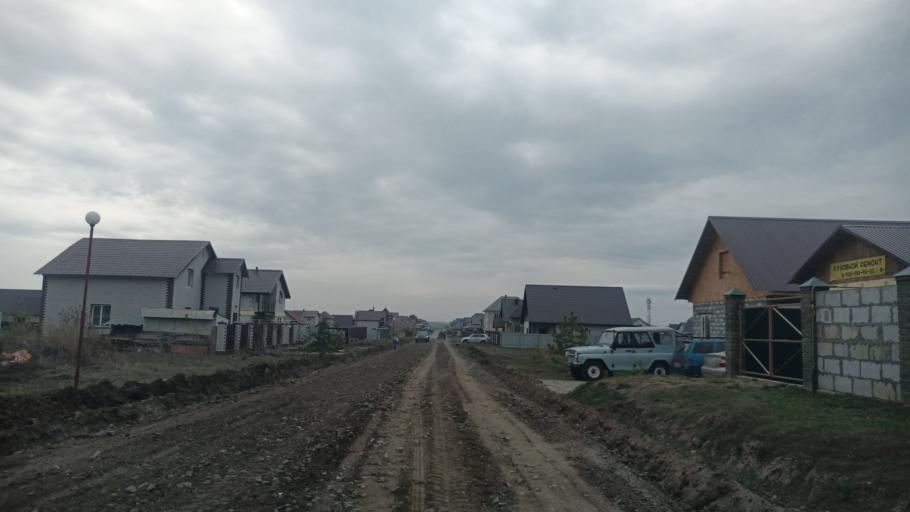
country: RU
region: Altai Krai
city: Yuzhnyy
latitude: 53.2267
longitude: 83.6910
